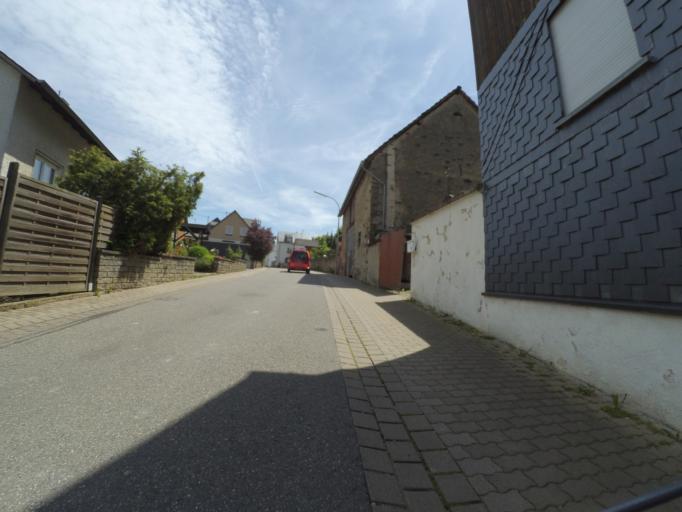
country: DE
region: Rheinland-Pfalz
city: Lonnig
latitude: 50.3101
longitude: 7.4096
